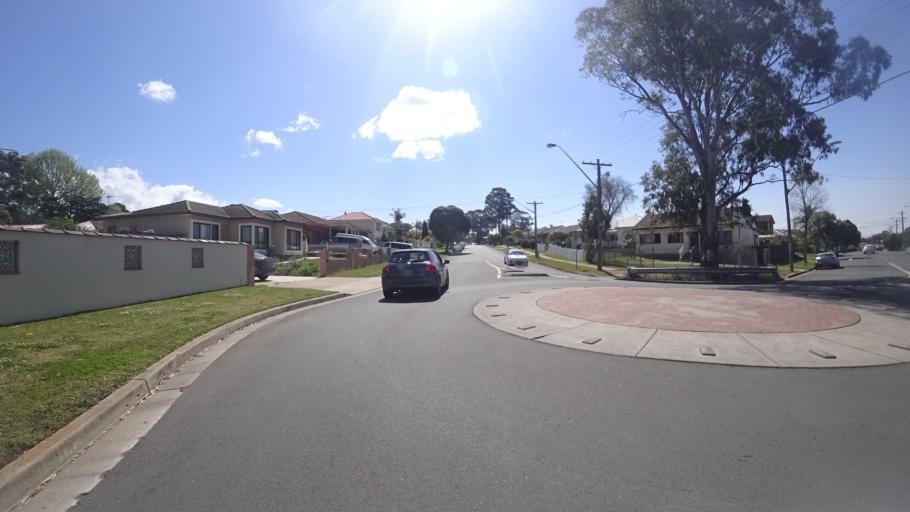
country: AU
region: New South Wales
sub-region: Fairfield
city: Cabramatta West
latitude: -33.9115
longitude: 150.9059
